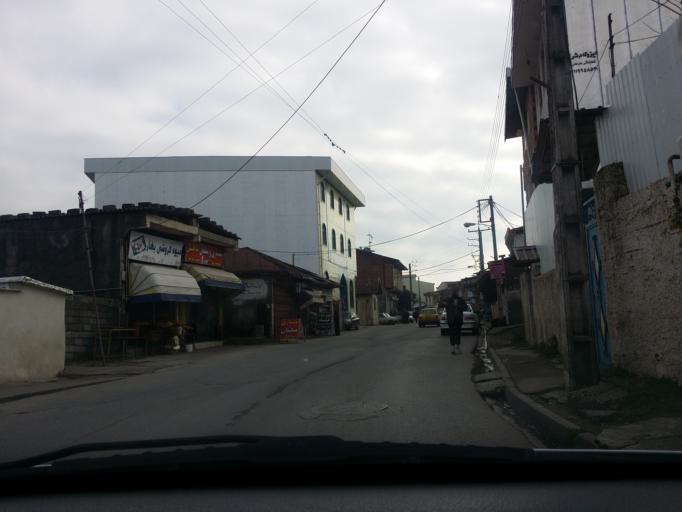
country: IR
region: Mazandaran
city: Chalus
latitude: 36.6579
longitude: 51.4109
